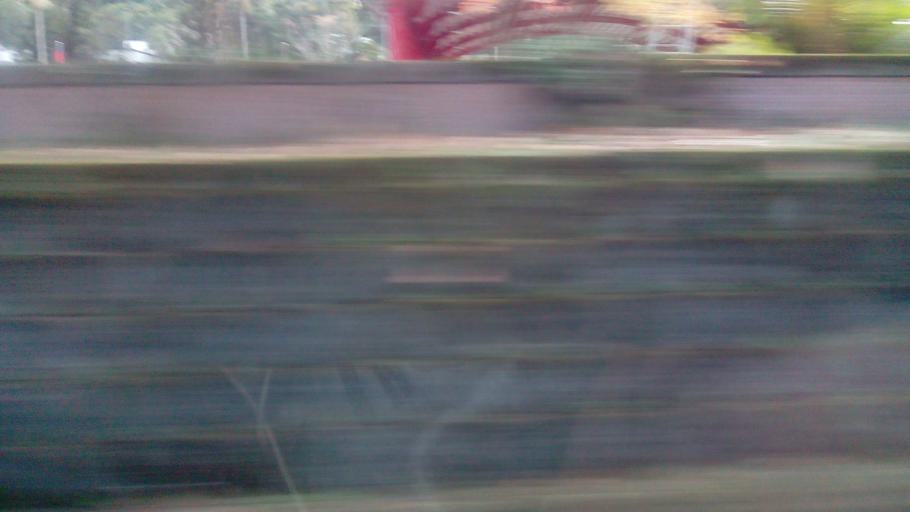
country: TW
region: Taiwan
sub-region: Yilan
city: Yilan
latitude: 24.5755
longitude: 121.4772
